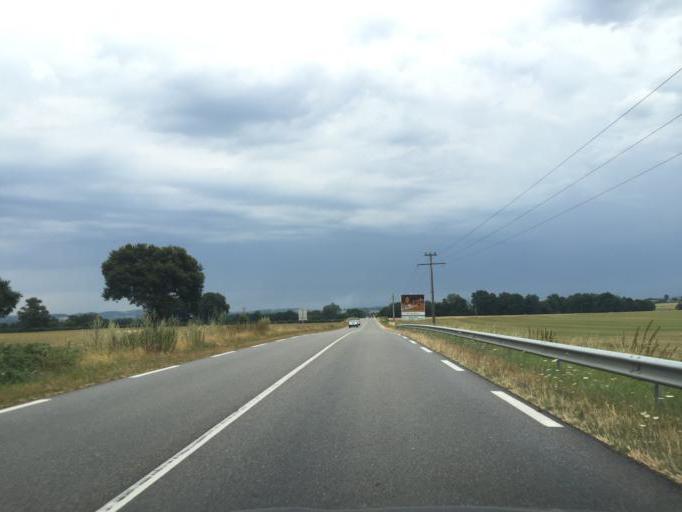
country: FR
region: Auvergne
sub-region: Departement de l'Allier
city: Lapalisse
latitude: 46.2482
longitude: 3.5922
